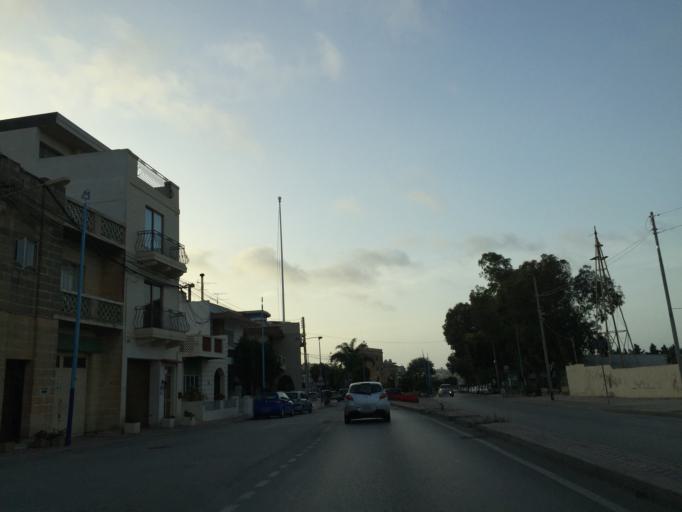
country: MT
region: Saint Paul's Bay
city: San Pawl il-Bahar
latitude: 35.9330
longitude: 14.4156
